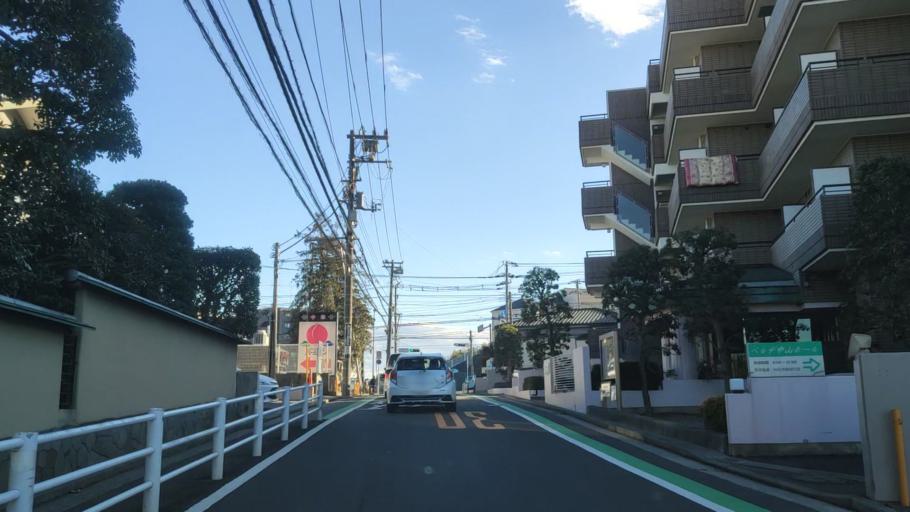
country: JP
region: Tokyo
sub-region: Machida-shi
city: Machida
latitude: 35.5135
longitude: 139.5482
